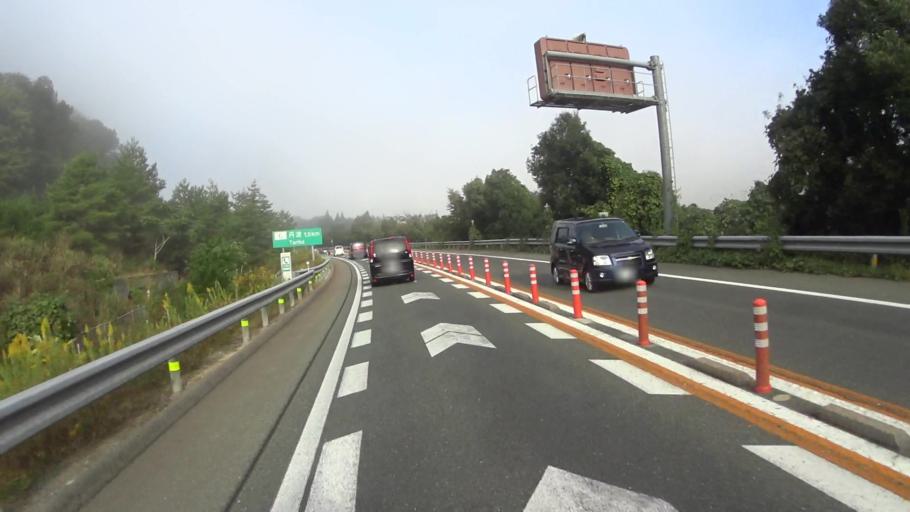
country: JP
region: Kyoto
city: Kameoka
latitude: 35.1429
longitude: 135.4434
